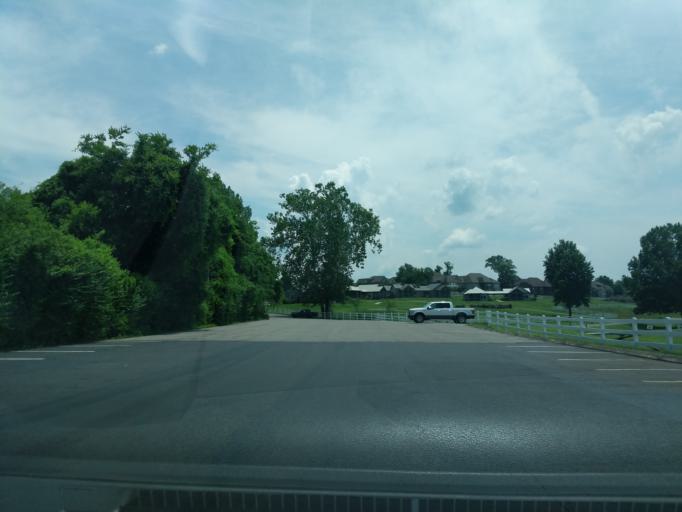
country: US
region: Tennessee
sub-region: Davidson County
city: Lakewood
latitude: 36.2343
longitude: -86.6370
